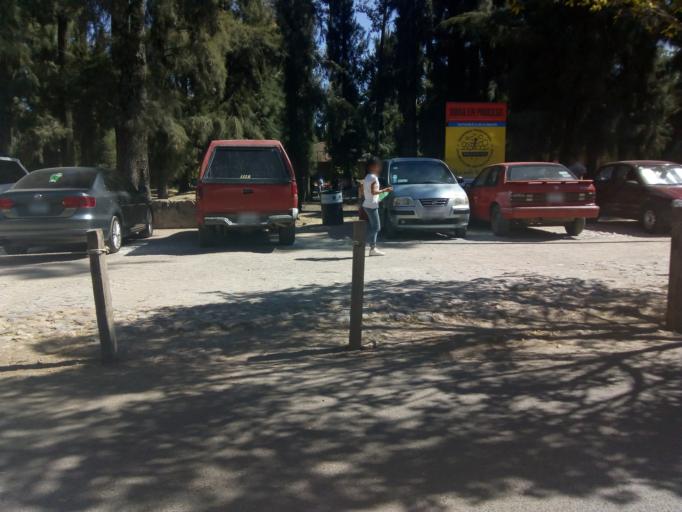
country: MX
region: Guanajuato
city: Leon
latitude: 21.1729
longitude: -101.6889
